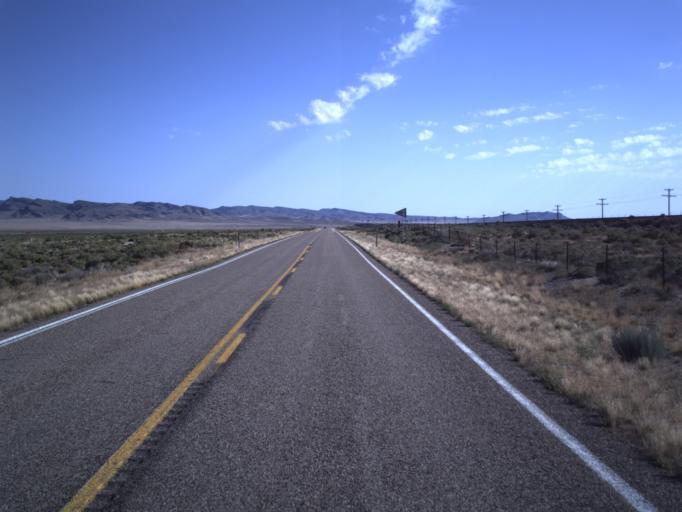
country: US
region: Utah
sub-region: Beaver County
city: Milford
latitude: 38.6765
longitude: -112.9792
